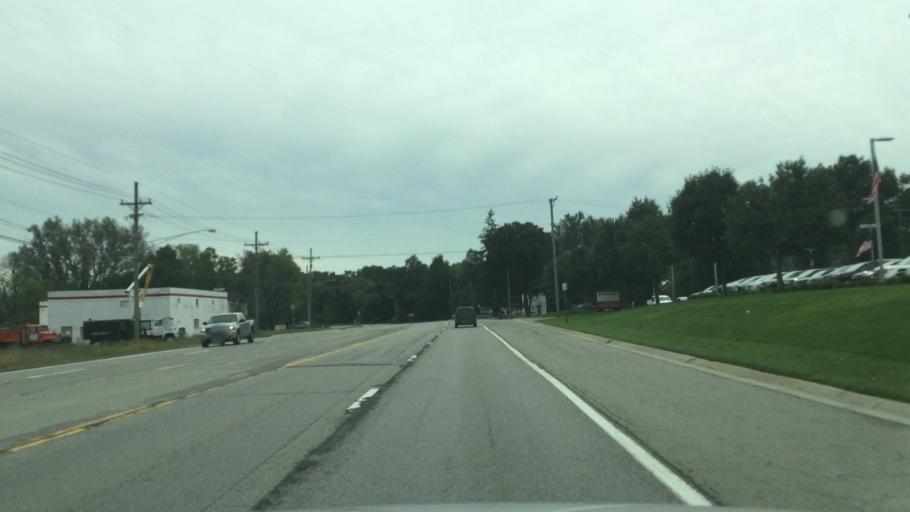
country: US
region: Michigan
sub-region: Oakland County
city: Clarkston
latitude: 42.7542
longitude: -83.4798
